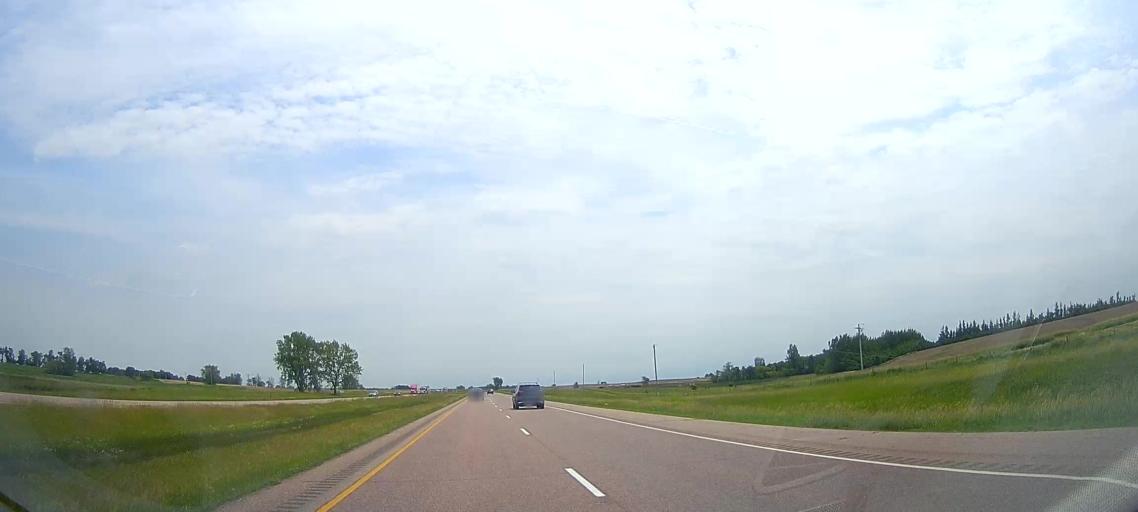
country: US
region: South Dakota
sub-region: Minnehaha County
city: Hartford
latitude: 43.6168
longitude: -97.0435
